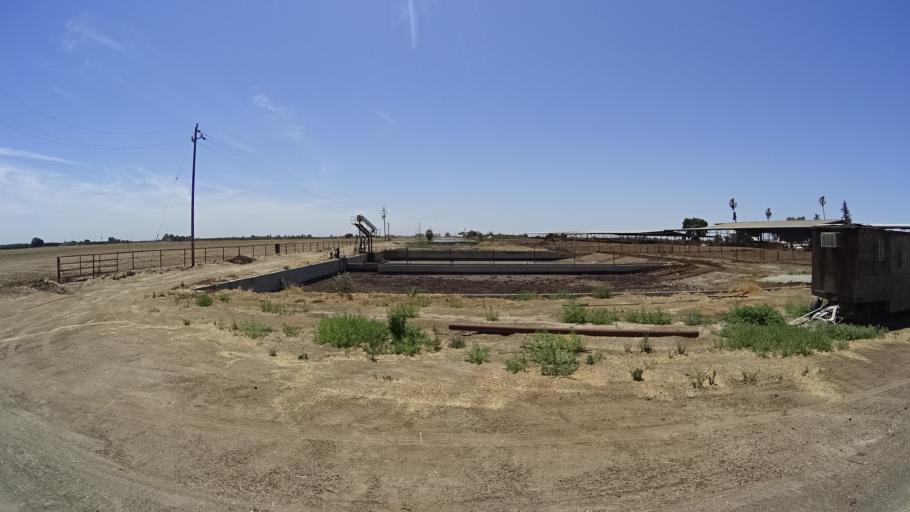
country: US
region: California
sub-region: Kings County
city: Armona
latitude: 36.3390
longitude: -119.7517
